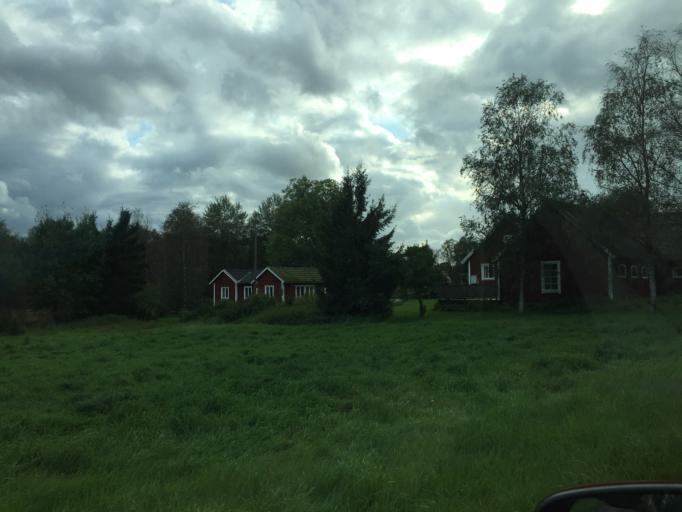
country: SE
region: Skane
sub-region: Perstorps Kommun
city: Perstorp
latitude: 56.2210
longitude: 13.3615
